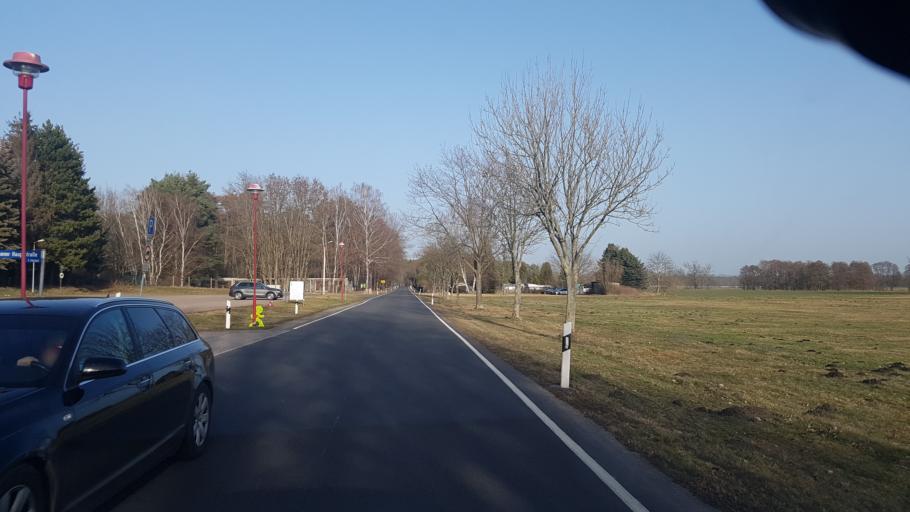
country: DE
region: Brandenburg
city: Heinersbruck
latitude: 51.7061
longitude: 14.4653
